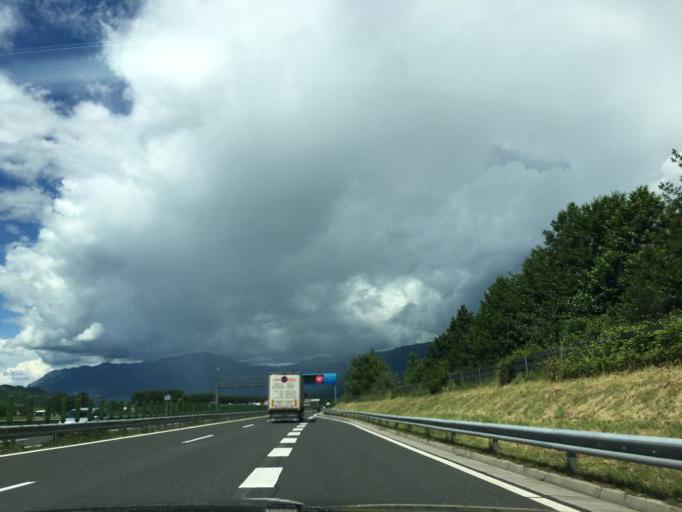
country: SI
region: Vipava
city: Vipava
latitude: 45.8312
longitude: 13.9568
